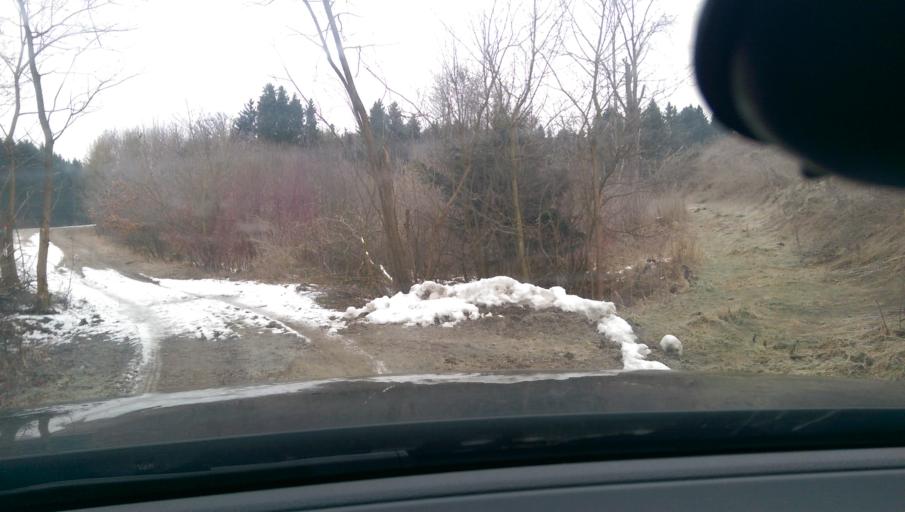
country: DE
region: Bavaria
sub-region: Lower Bavaria
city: Hutthurm
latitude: 48.6636
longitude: 13.4797
